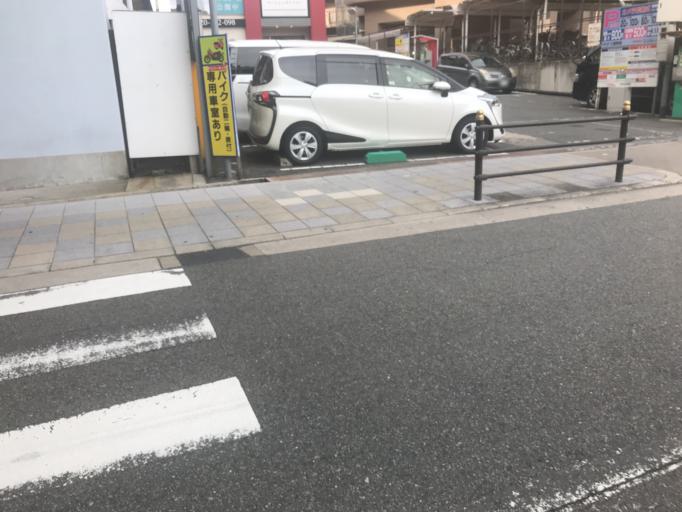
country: JP
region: Osaka
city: Suita
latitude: 34.7381
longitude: 135.4830
